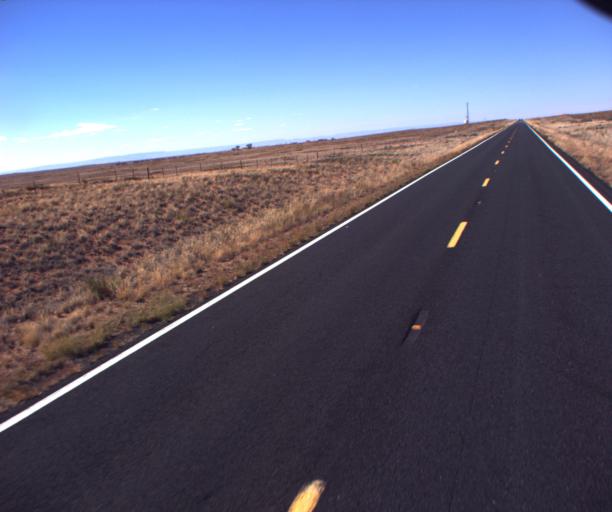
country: US
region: Arizona
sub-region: Coconino County
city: Tuba City
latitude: 35.9883
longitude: -111.0065
